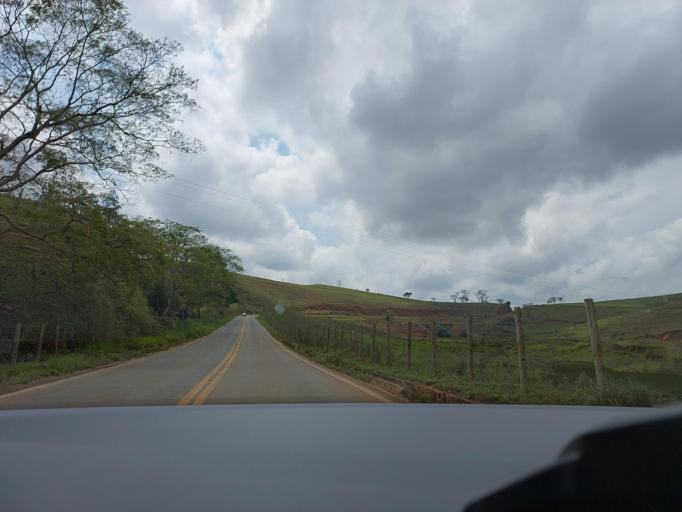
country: BR
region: Minas Gerais
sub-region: Ponte Nova
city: Ponte Nova
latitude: -20.3846
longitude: -42.8815
